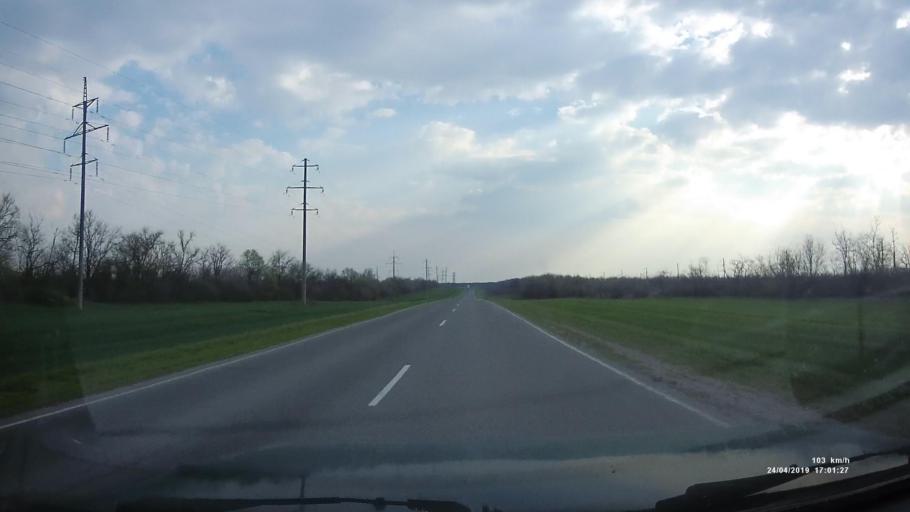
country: RU
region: Rostov
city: Sal'sk
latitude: 46.5921
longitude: 41.6252
